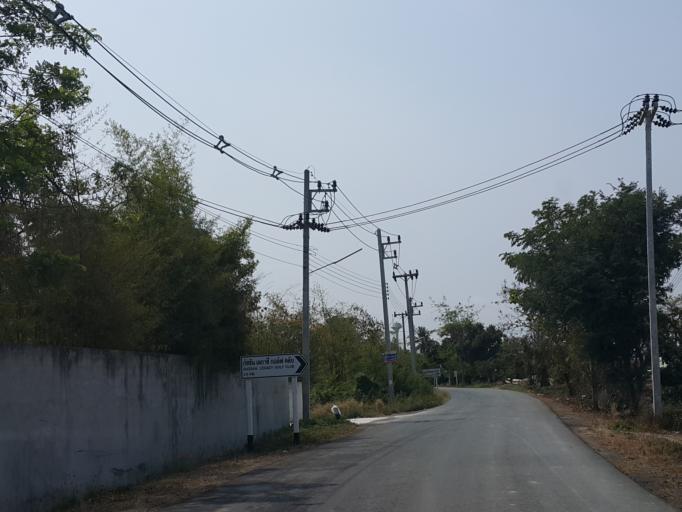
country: TH
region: Lamphun
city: Ban Thi
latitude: 18.6668
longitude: 99.0988
